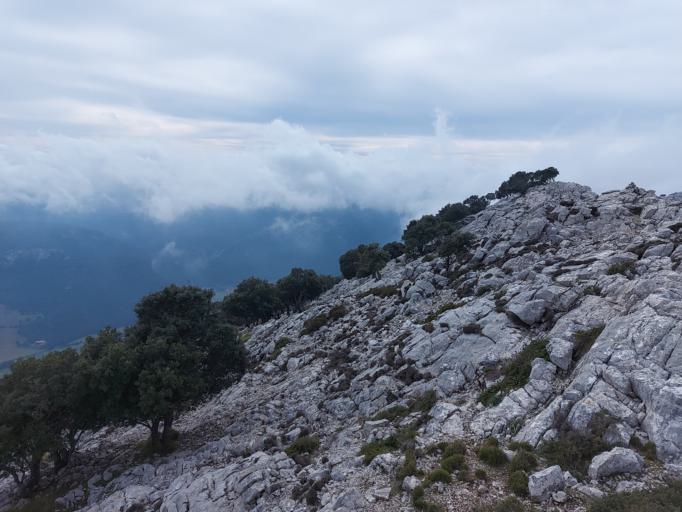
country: ES
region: Balearic Islands
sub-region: Illes Balears
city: Fornalutx
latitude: 39.7488
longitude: 2.7478
